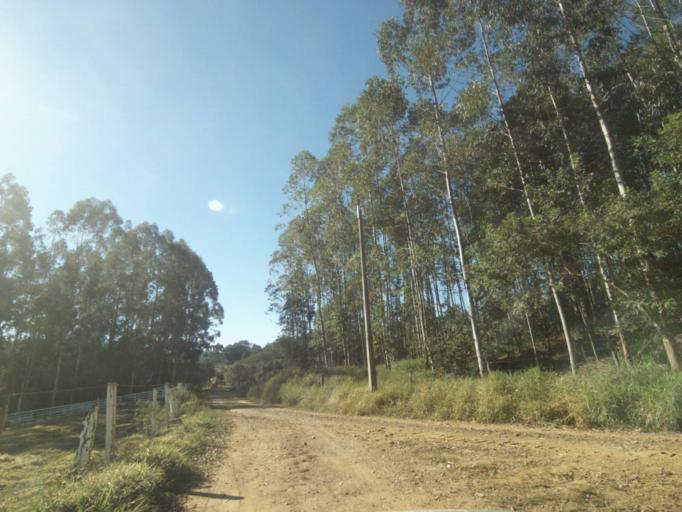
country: BR
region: Parana
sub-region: Tibagi
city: Tibagi
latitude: -24.5555
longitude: -50.5184
